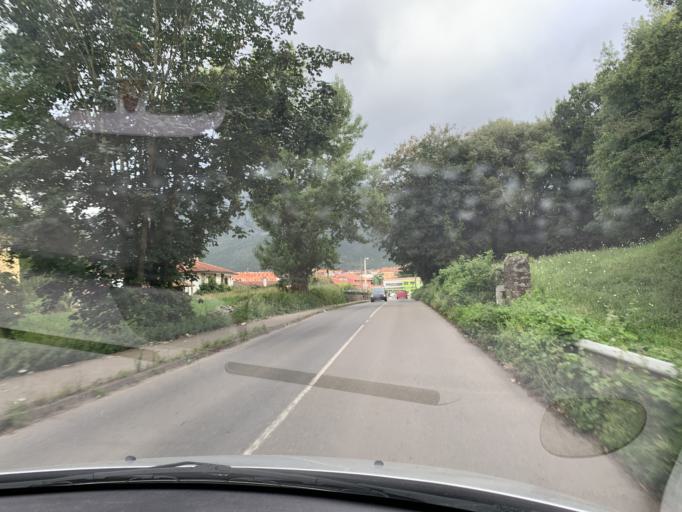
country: ES
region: Asturias
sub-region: Province of Asturias
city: Llanes
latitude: 43.4288
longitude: -4.8624
